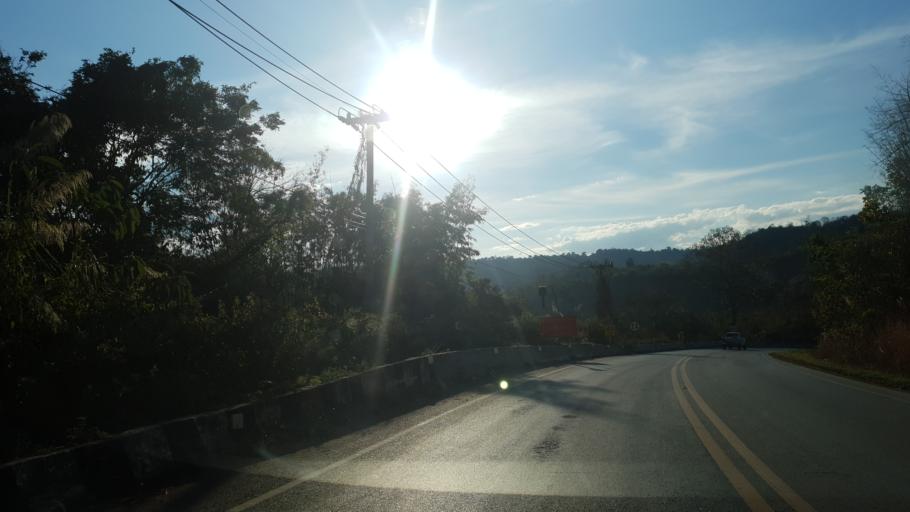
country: TH
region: Loei
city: Dan Sai
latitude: 17.2304
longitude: 101.0792
